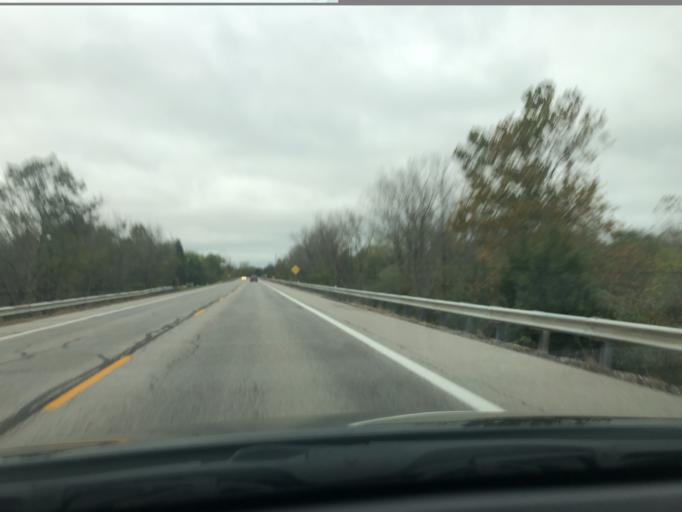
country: US
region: Ohio
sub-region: Union County
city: New California
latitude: 40.2712
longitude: -83.2208
